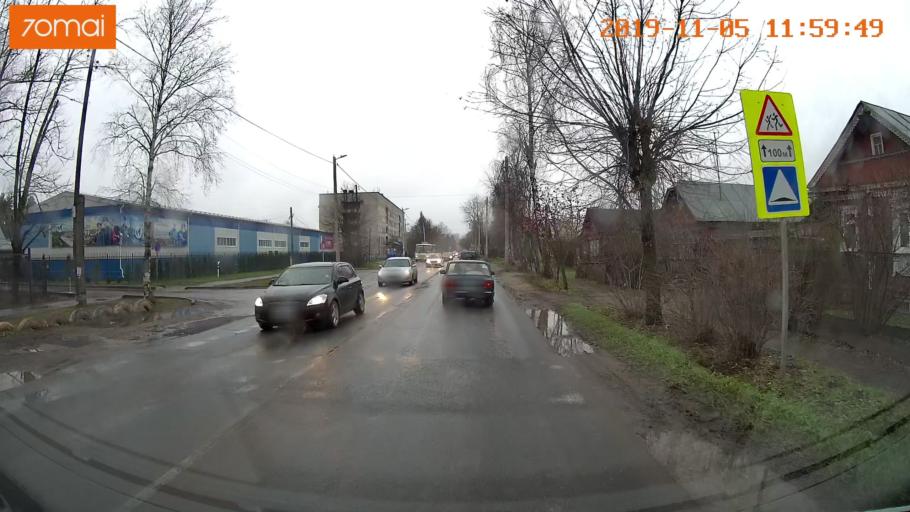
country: RU
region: Ivanovo
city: Kokhma
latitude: 56.9774
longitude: 41.0498
